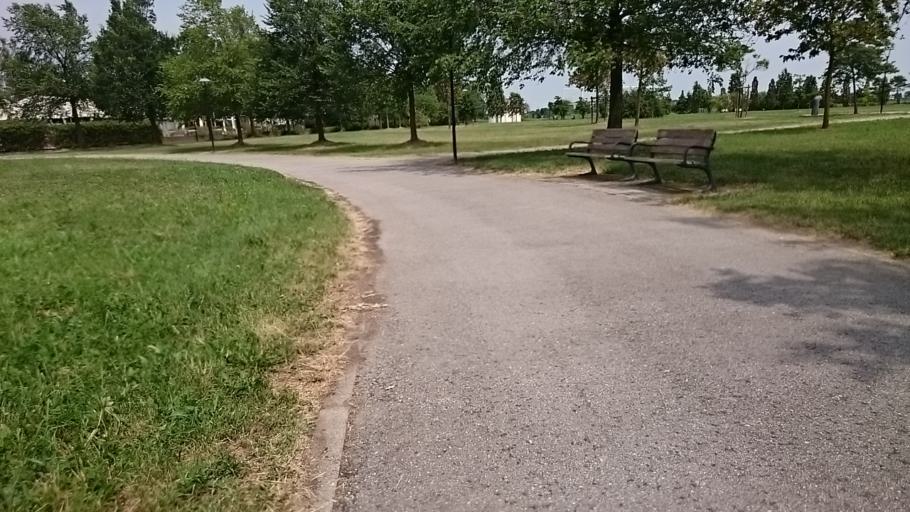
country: IT
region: Veneto
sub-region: Provincia di Venezia
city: Campalto
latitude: 45.4687
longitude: 12.2791
